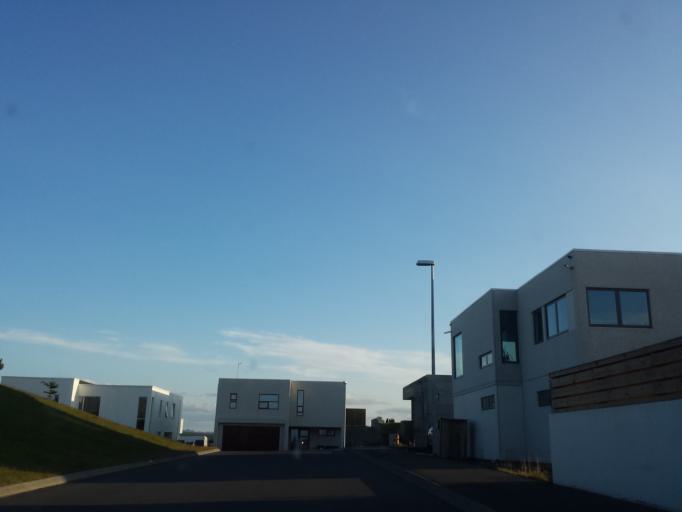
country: IS
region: Capital Region
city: Kopavogur
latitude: 64.0915
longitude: -21.8694
